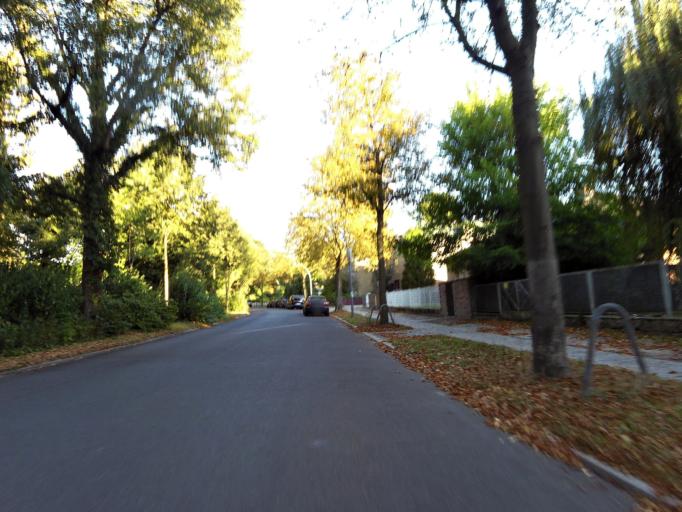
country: DE
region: Berlin
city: Dahlem
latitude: 52.4649
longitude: 13.2911
